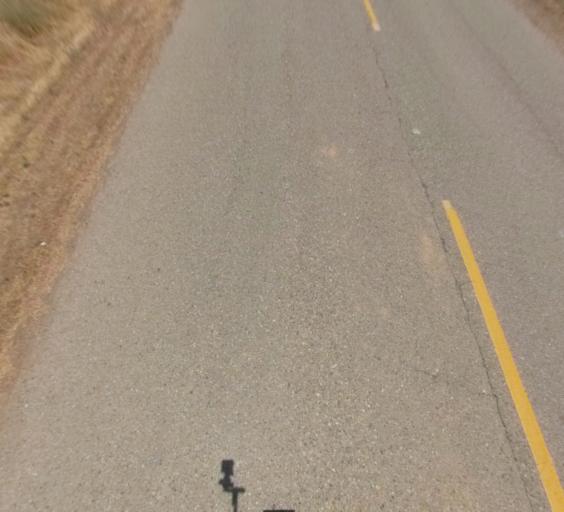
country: US
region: California
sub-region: Madera County
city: Madera Acres
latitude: 37.0631
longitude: -120.0112
